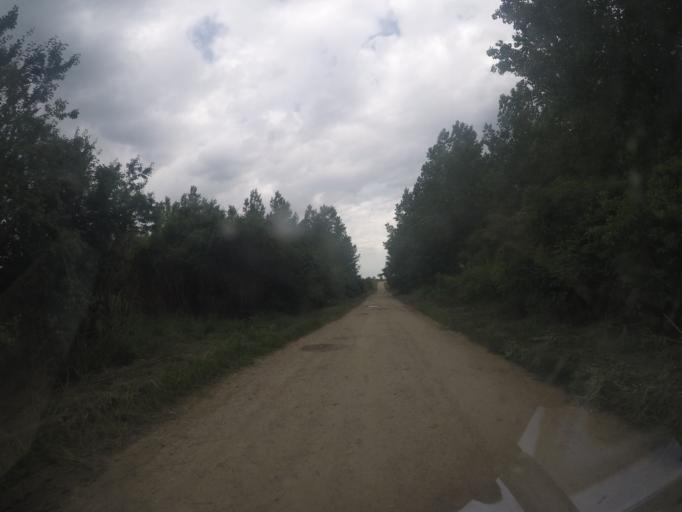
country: RS
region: Central Serbia
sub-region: Belgrade
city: Zemun
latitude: 44.8925
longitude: 20.3796
